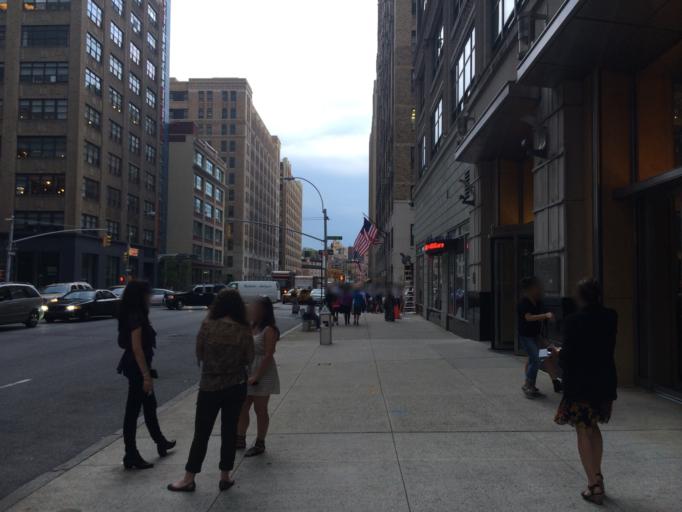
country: US
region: New York
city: New York City
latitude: 40.7267
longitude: -74.0055
